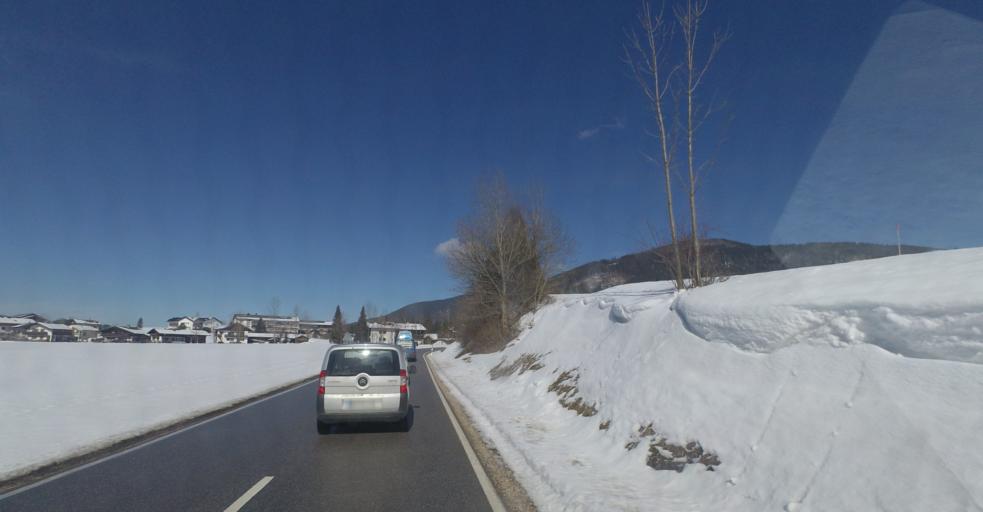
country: DE
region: Bavaria
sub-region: Upper Bavaria
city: Inzell
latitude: 47.7650
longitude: 12.7656
